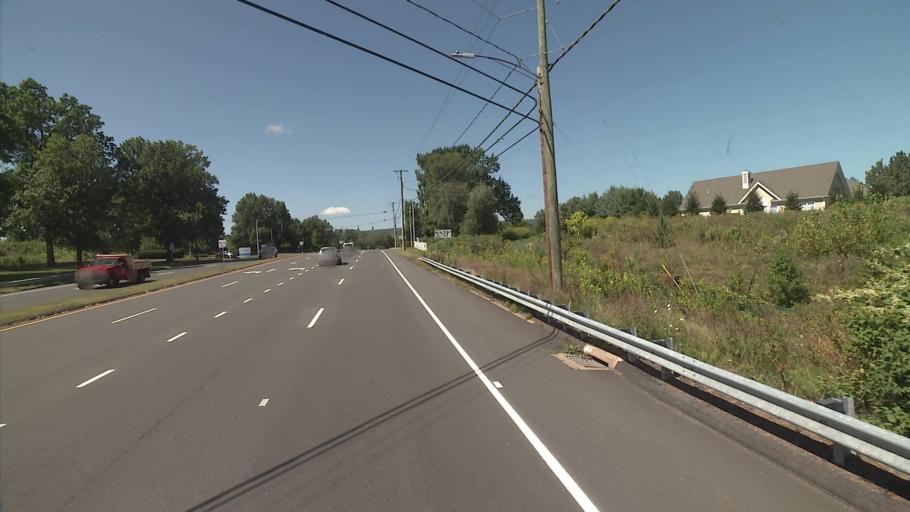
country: US
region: Connecticut
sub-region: Hartford County
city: Blue Hills
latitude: 41.8168
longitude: -72.7422
